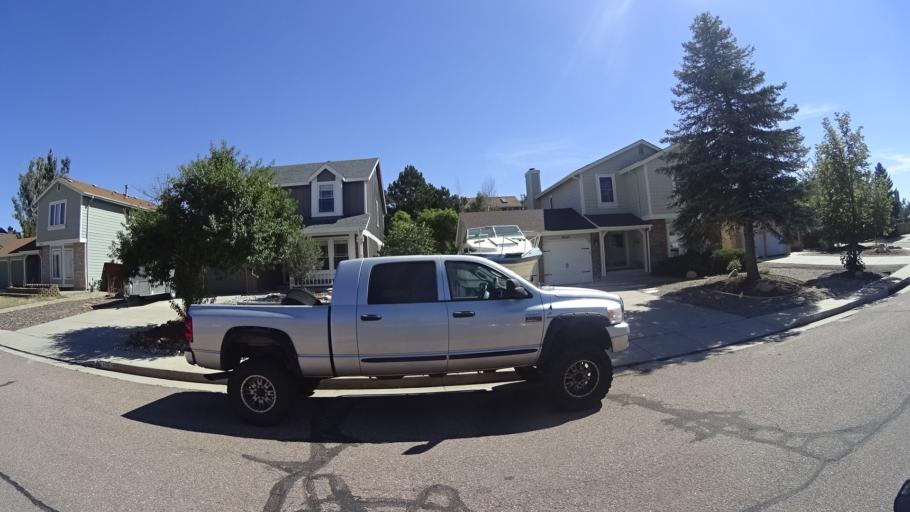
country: US
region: Colorado
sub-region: El Paso County
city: Black Forest
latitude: 38.9477
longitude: -104.7517
